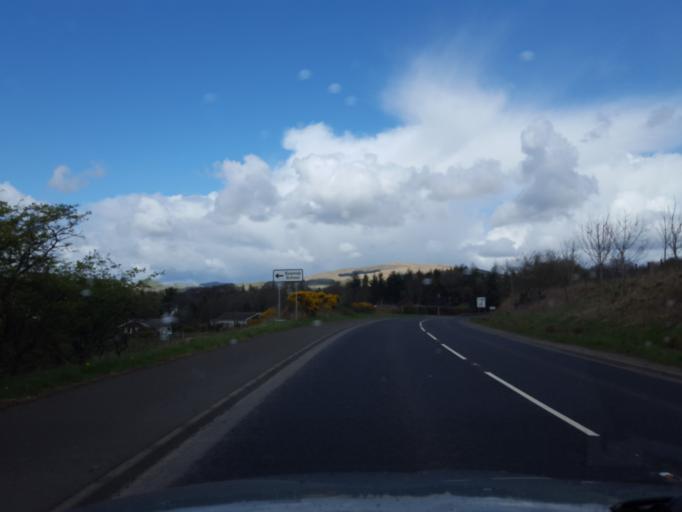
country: GB
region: Scotland
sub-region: Fife
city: Saline
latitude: 56.1729
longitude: -3.5820
